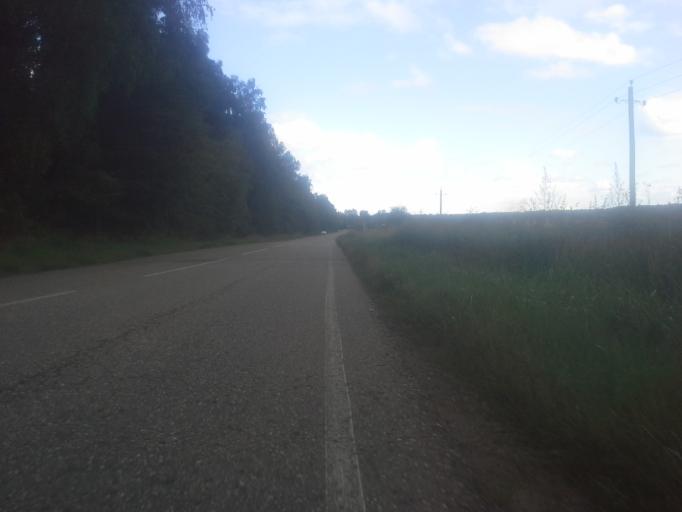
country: RU
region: Moskovskaya
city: Kolyubakino
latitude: 55.6546
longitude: 36.6111
